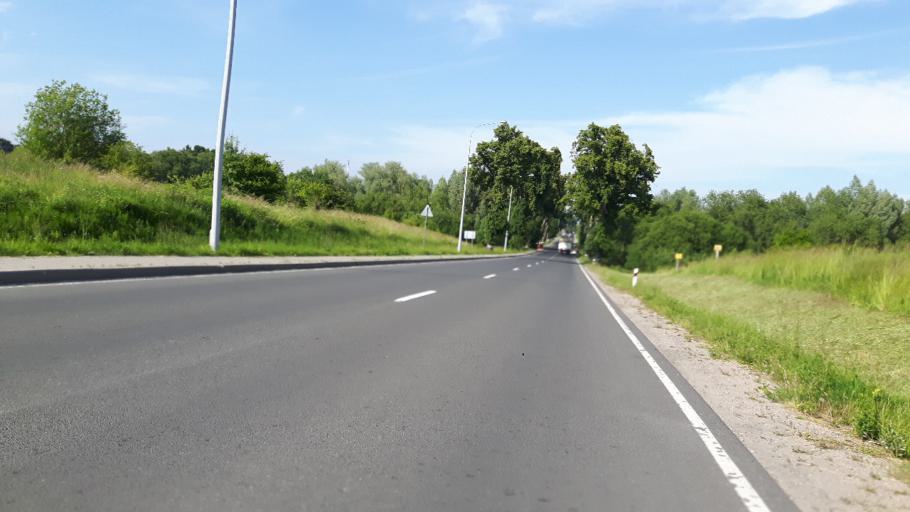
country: RU
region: Kaliningrad
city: Mamonovo
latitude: 54.4535
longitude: 19.9212
